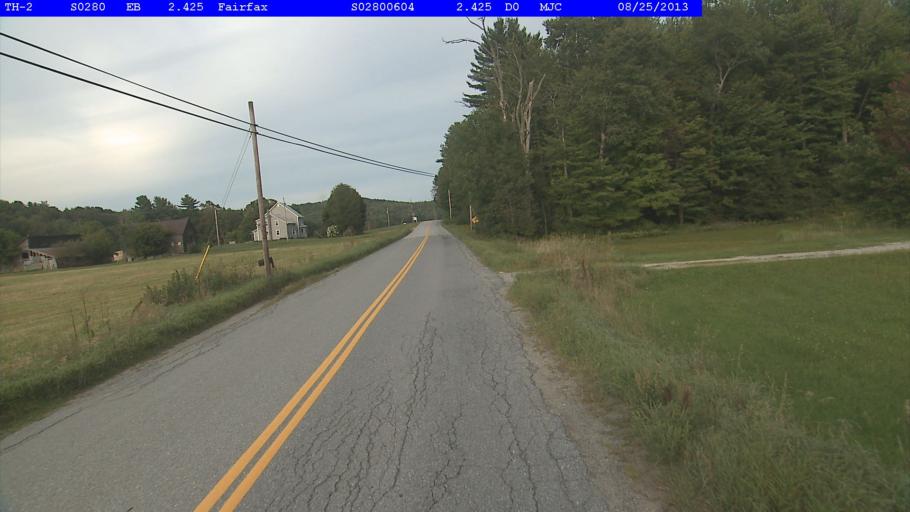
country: US
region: Vermont
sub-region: Chittenden County
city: Milton
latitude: 44.6725
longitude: -72.9636
